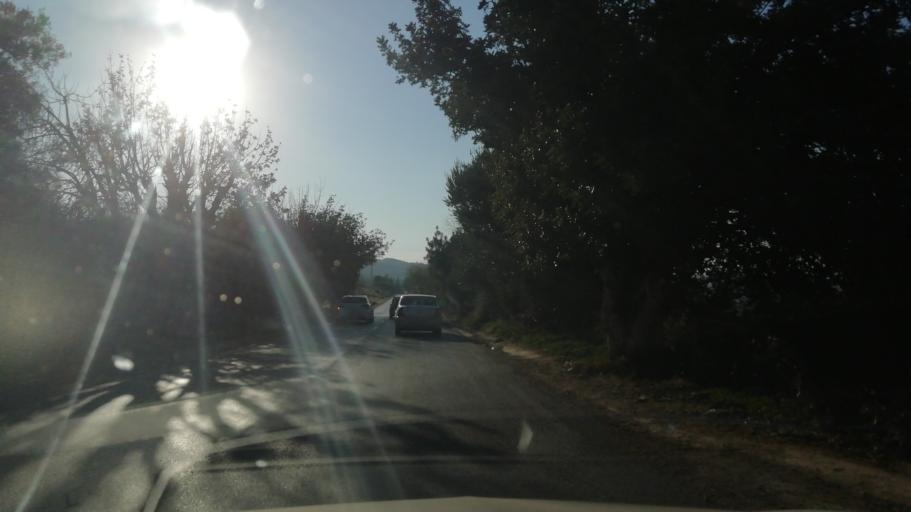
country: DZ
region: Tlemcen
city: Beni Mester
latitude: 34.8647
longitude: -1.4310
